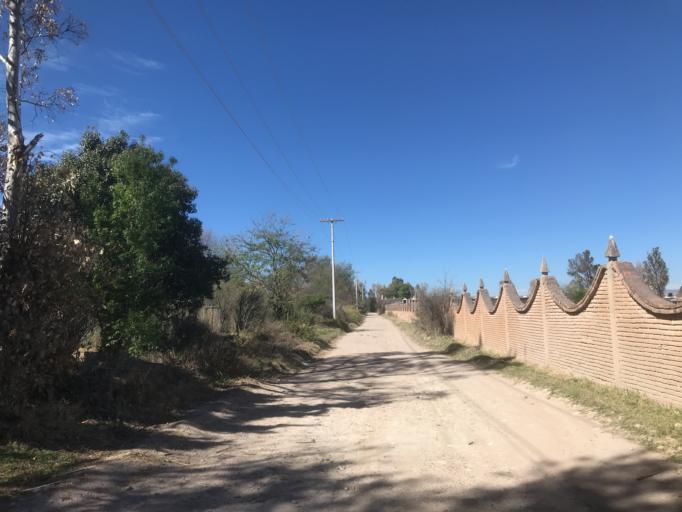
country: MX
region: Durango
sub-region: Durango
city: Sebastian Lerdo de Tejada
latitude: 23.9750
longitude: -104.6227
